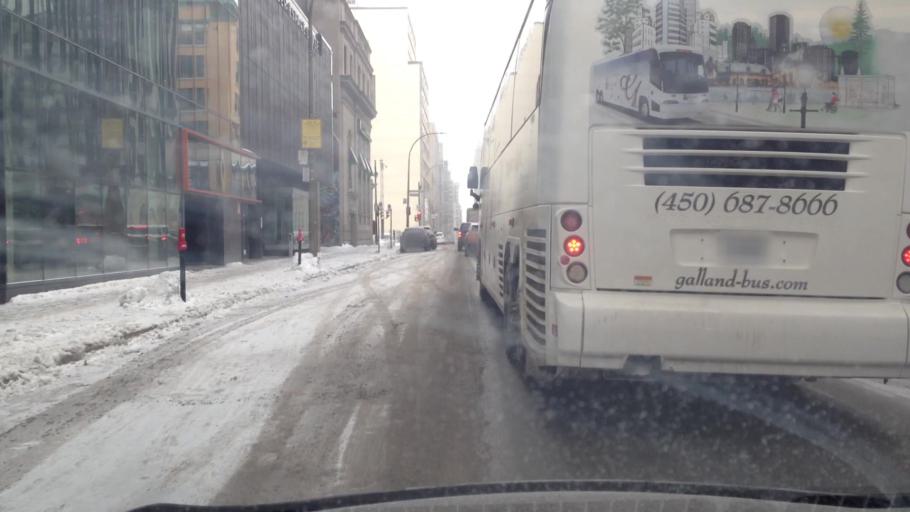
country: CA
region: Quebec
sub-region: Montreal
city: Montreal
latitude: 45.5068
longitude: -73.5681
